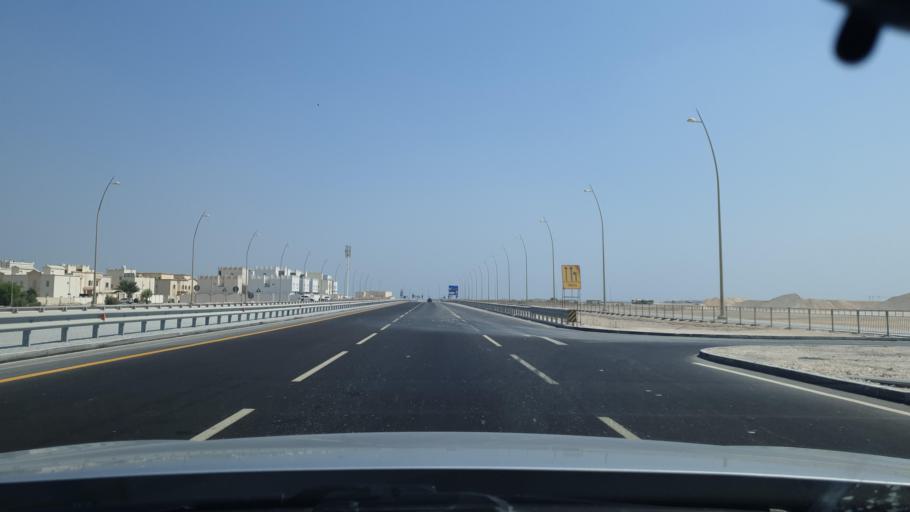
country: QA
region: Al Khawr
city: Al Khawr
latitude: 25.6653
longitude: 51.5108
